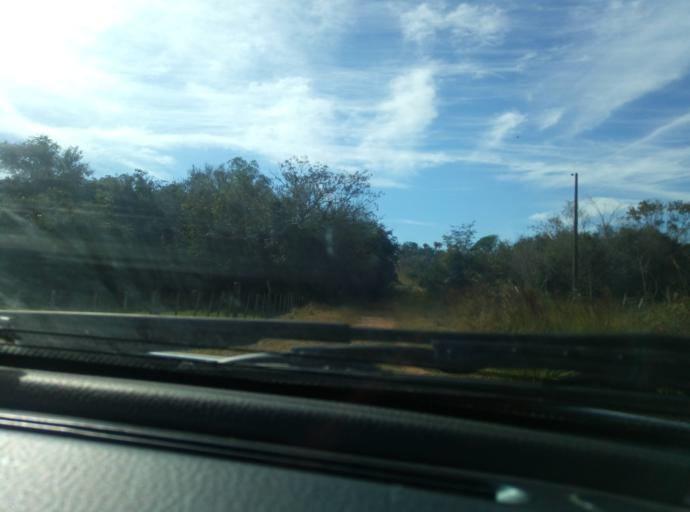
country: PY
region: Caaguazu
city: Carayao
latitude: -25.1652
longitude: -56.2927
